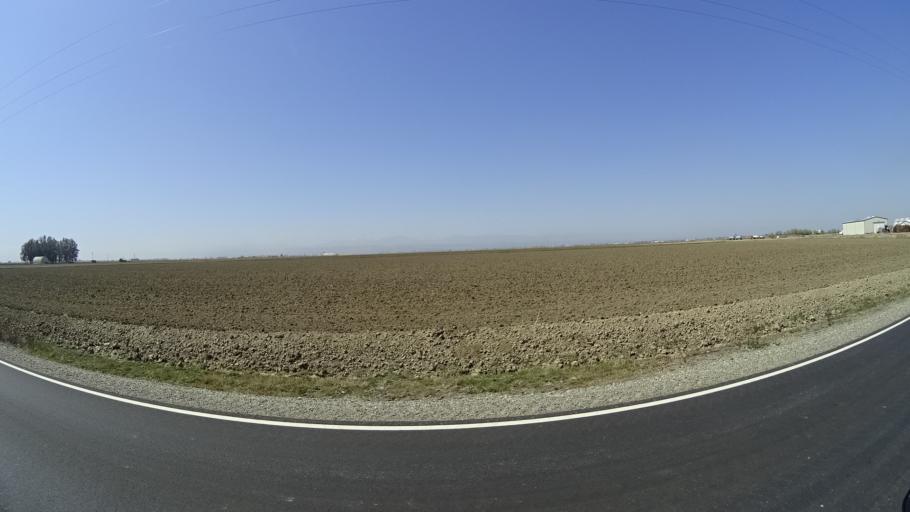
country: US
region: California
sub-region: Glenn County
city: Willows
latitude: 39.4783
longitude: -122.1365
